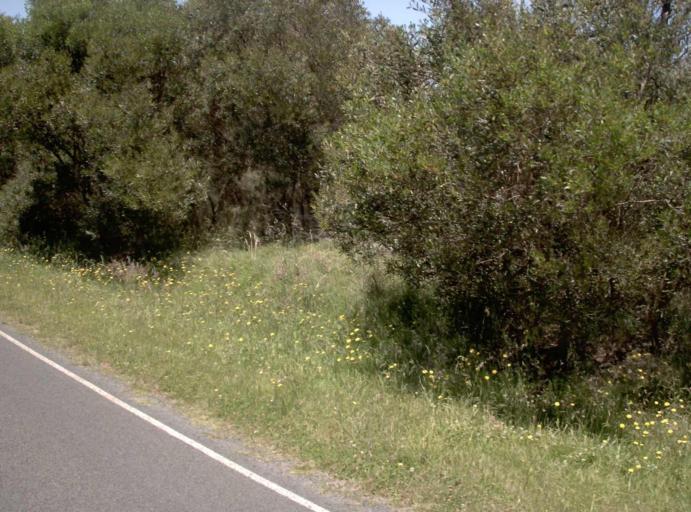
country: AU
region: Victoria
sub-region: Latrobe
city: Morwell
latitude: -38.7953
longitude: 146.1833
